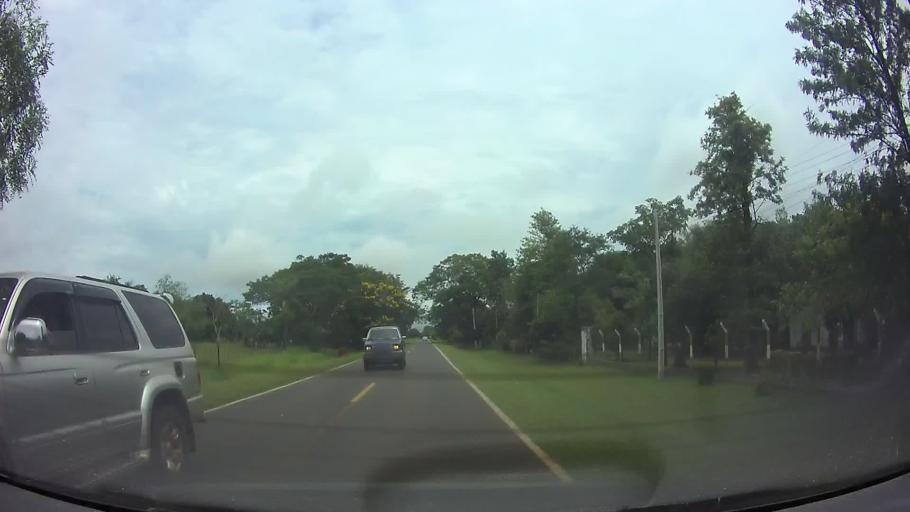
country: PY
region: Paraguari
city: Ybycui
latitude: -25.9849
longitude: -57.0657
